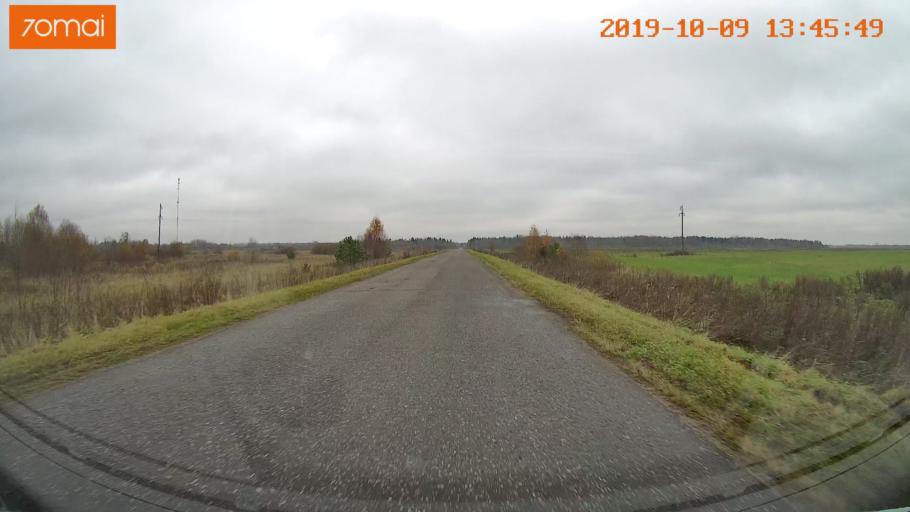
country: RU
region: Kostroma
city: Buy
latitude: 58.3777
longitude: 41.2130
